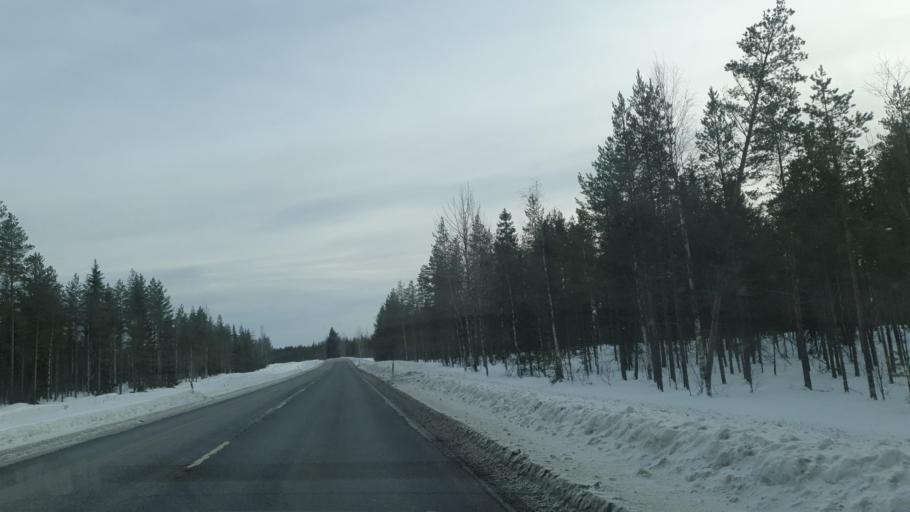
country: FI
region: Kainuu
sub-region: Kajaani
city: Vuolijoki
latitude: 64.5223
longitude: 27.2754
